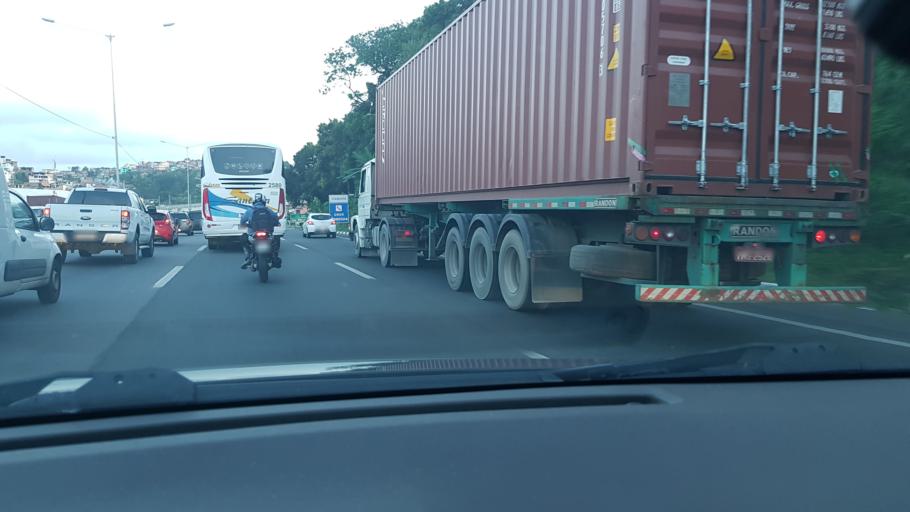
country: BR
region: Bahia
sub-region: Salvador
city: Salvador
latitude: -12.9390
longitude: -38.4719
